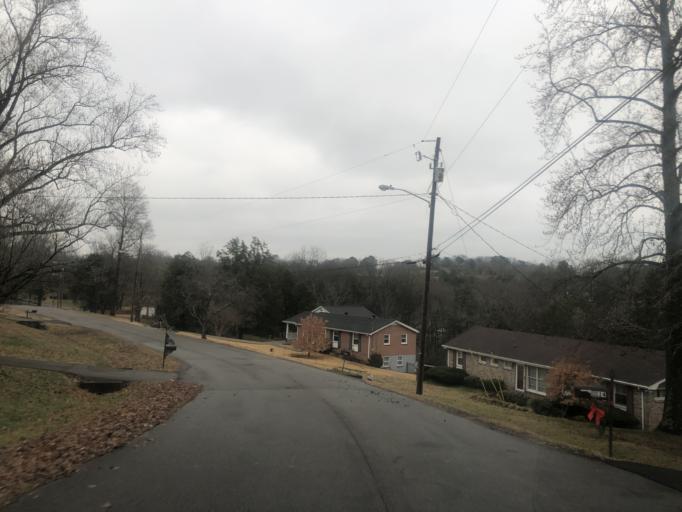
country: US
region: Tennessee
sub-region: Davidson County
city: Nashville
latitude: 36.1645
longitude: -86.6945
